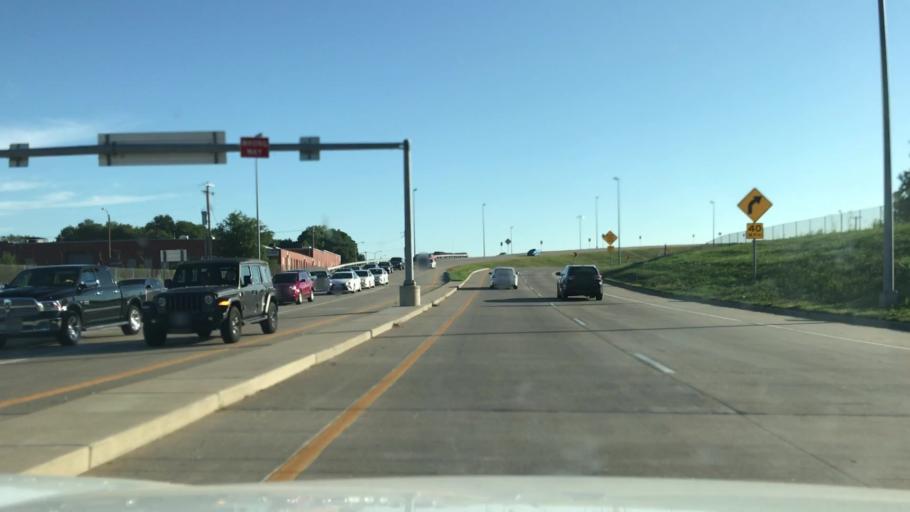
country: US
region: Missouri
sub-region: City of Saint Louis
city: St. Louis
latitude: 38.6411
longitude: -90.1915
